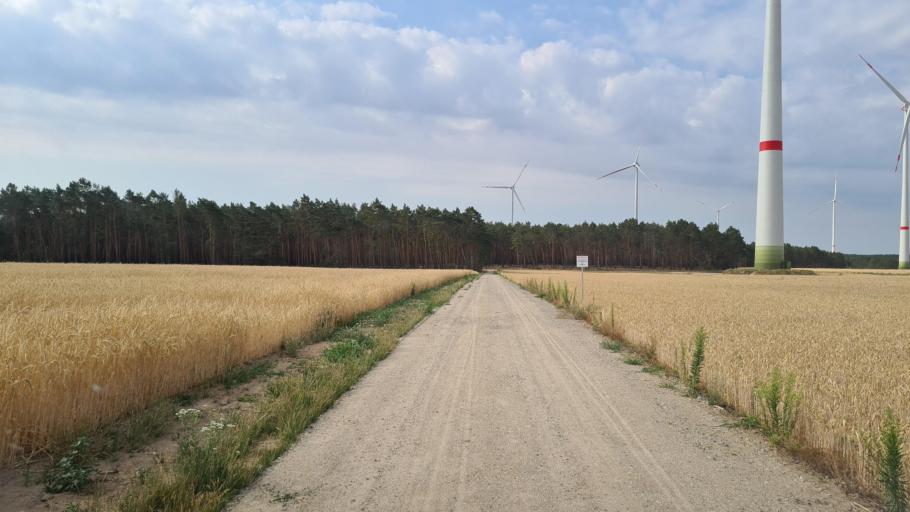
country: DE
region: Brandenburg
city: Linthe
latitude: 52.1044
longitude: 12.8086
